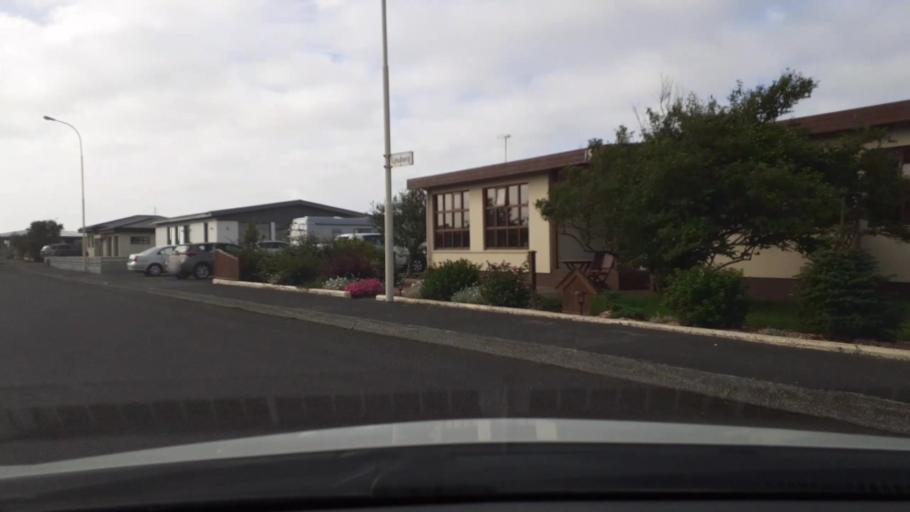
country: IS
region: South
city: THorlakshoefn
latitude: 63.8530
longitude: -21.3916
